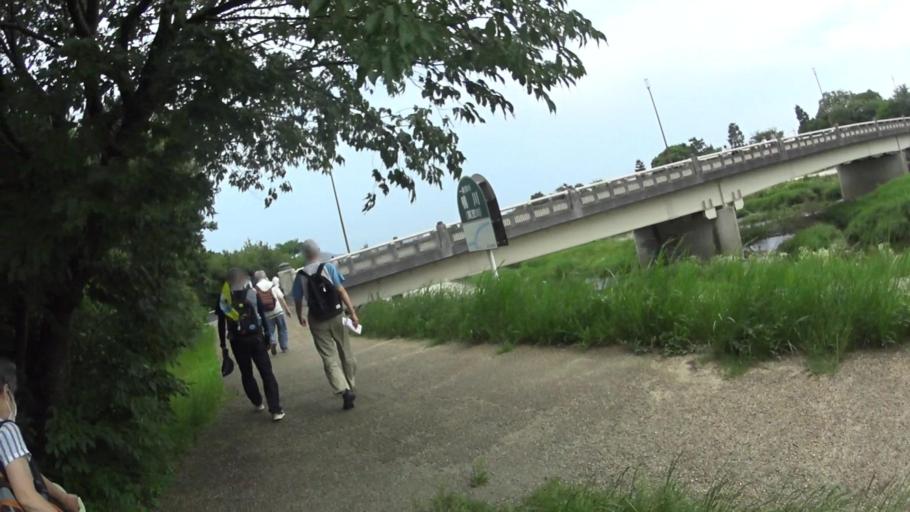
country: JP
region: Kyoto
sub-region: Kyoto-shi
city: Kamigyo-ku
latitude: 35.0389
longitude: 135.7674
